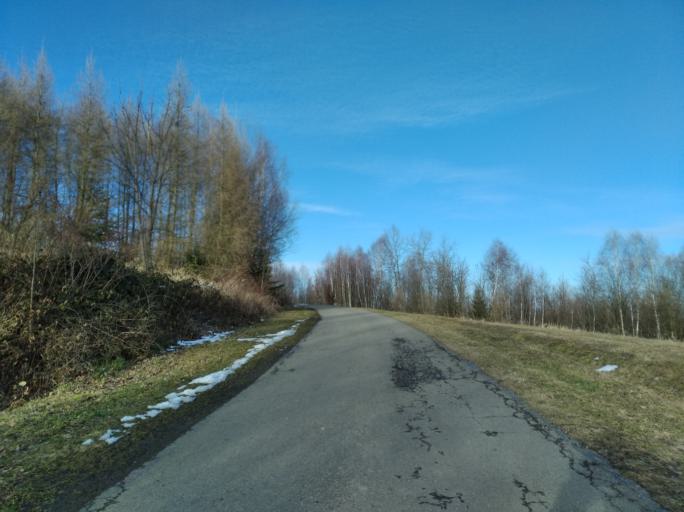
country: PL
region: Subcarpathian Voivodeship
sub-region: Powiat strzyzowski
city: Gwoznica Gorna
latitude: 49.8185
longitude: 21.9900
